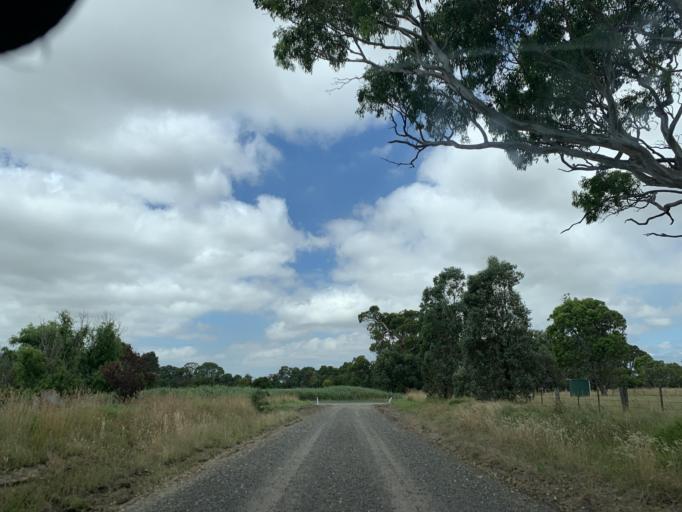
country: AU
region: Victoria
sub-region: Latrobe
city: Traralgon
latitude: -38.1162
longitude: 146.5754
